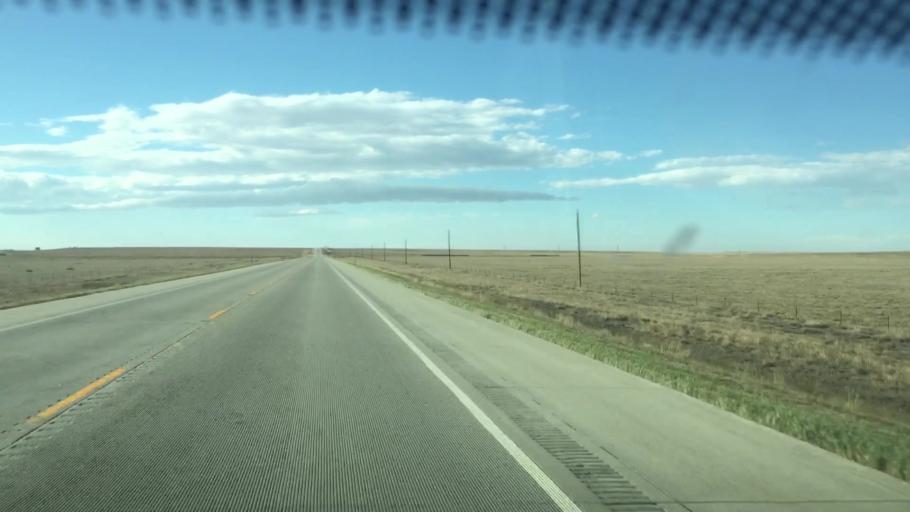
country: US
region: Colorado
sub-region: Lincoln County
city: Hugo
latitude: 39.0608
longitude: -103.3623
